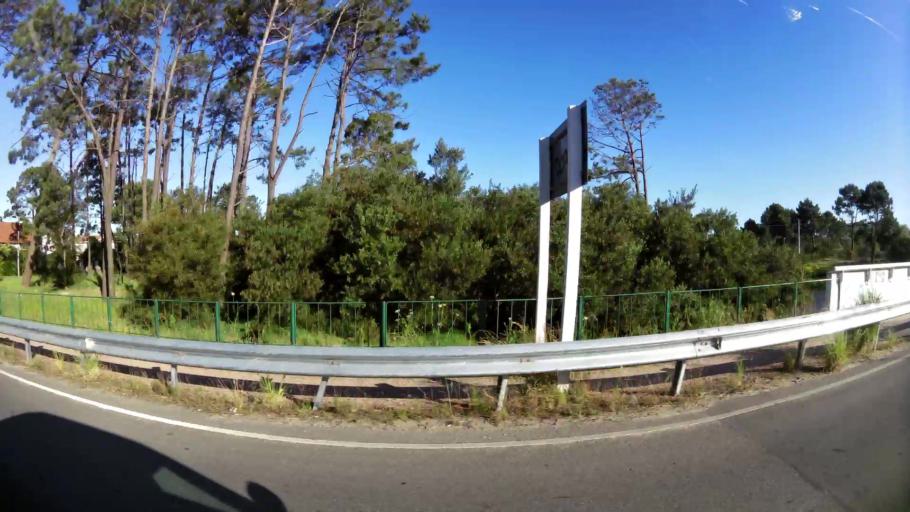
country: UY
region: Canelones
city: Barra de Carrasco
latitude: -34.8708
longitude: -56.0401
